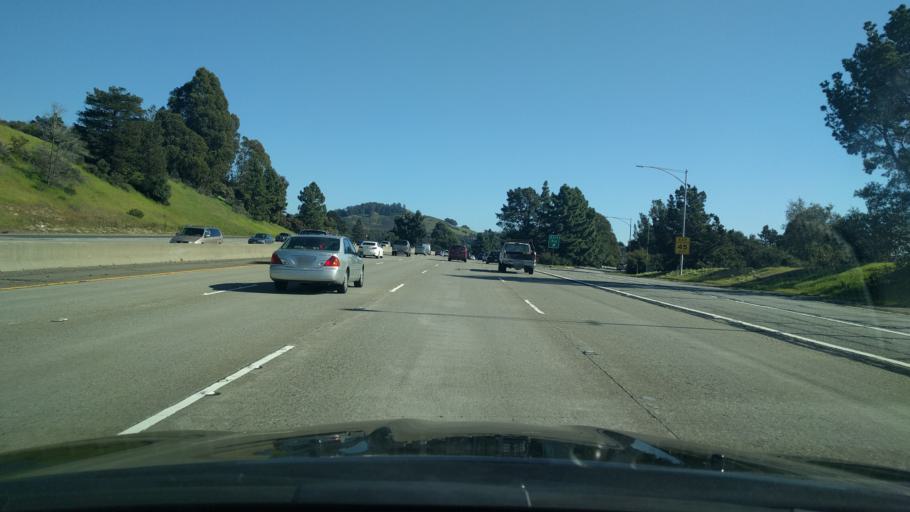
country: US
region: California
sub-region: Alameda County
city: San Leandro
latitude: 37.7395
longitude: -122.1432
